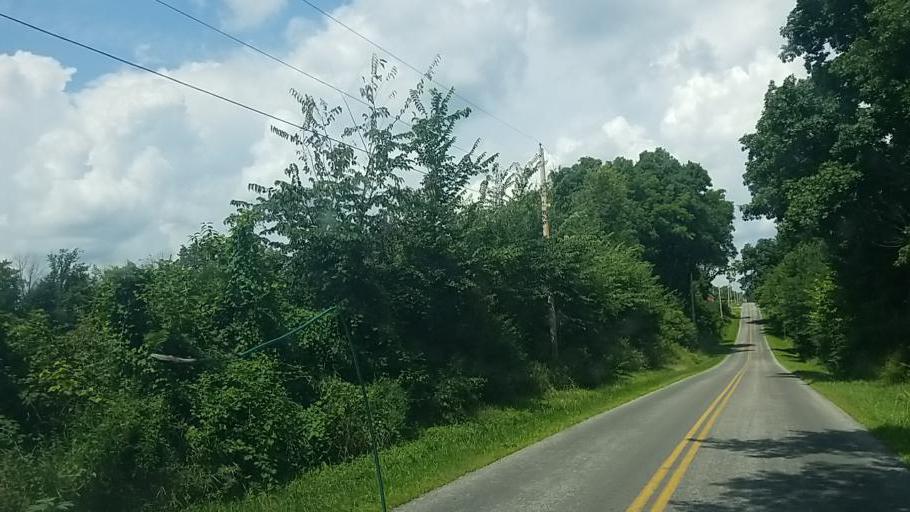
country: US
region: Ohio
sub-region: Medina County
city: Lodi
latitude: 41.0866
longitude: -82.0762
